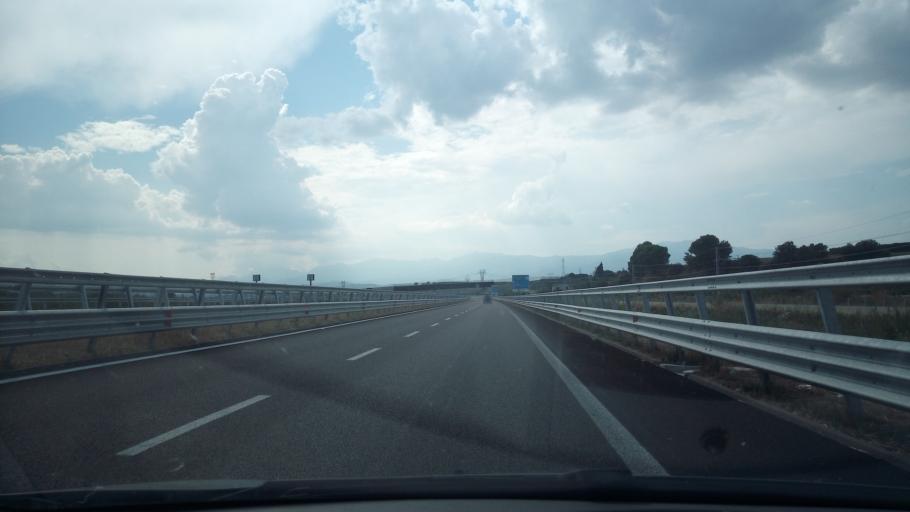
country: IT
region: Calabria
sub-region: Provincia di Cosenza
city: Doria
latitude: 39.7269
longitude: 16.3328
